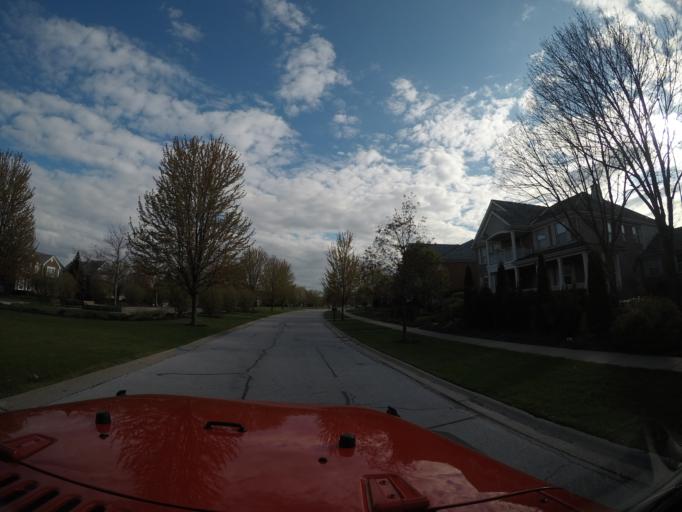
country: US
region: Illinois
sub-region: Cook County
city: Glenview
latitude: 42.0847
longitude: -87.8164
